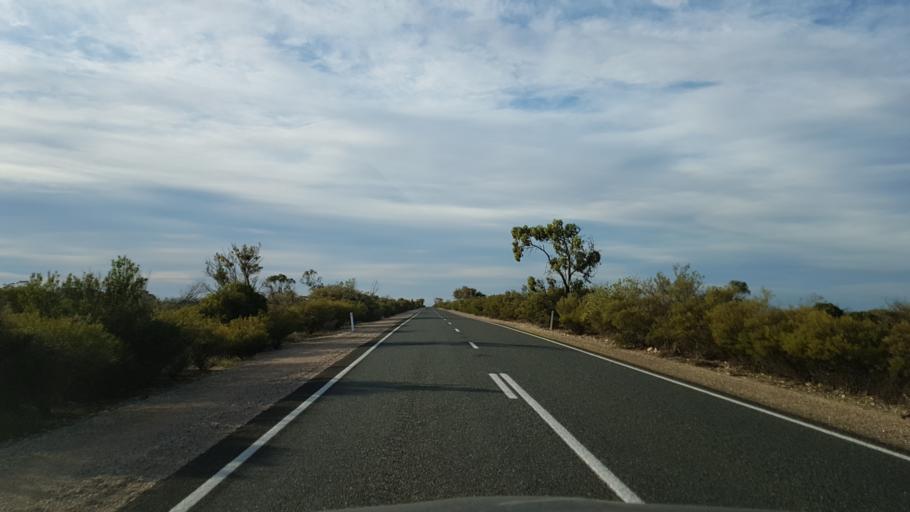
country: AU
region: South Australia
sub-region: Mid Murray
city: Mannum
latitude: -34.8379
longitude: 139.6096
